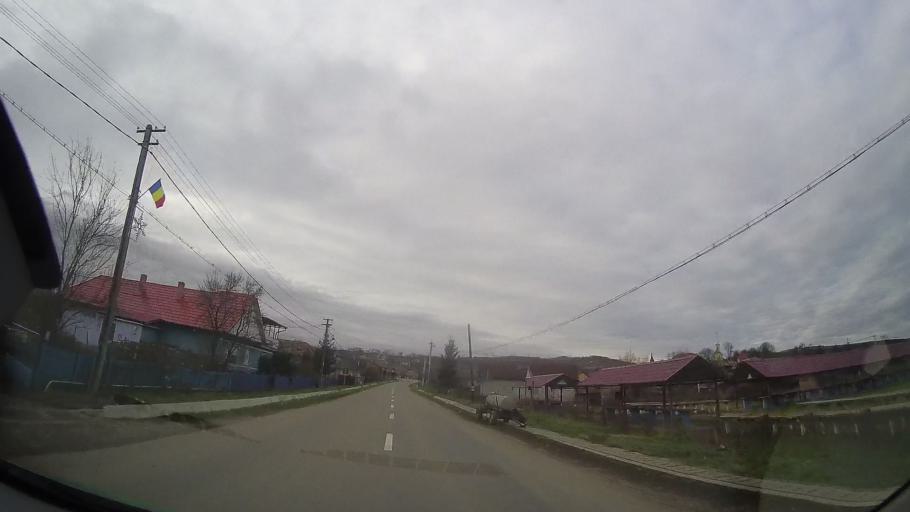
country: RO
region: Bistrita-Nasaud
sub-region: Comuna Milas
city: Milas
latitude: 46.8211
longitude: 24.4394
